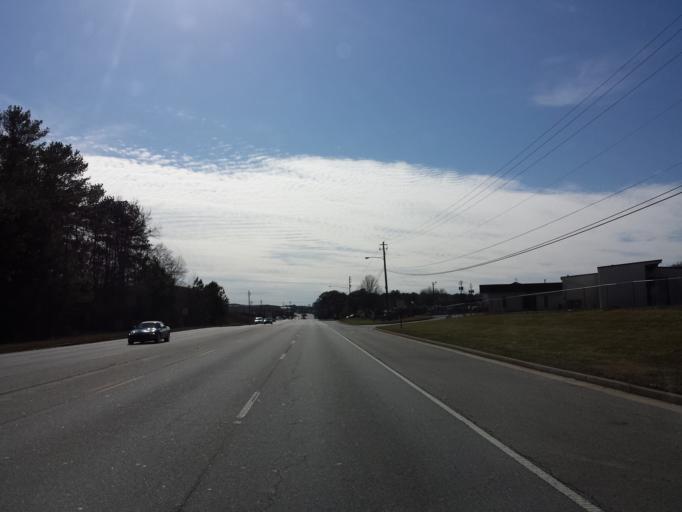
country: US
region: Georgia
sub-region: Cobb County
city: Kennesaw
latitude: 34.0190
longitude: -84.5969
